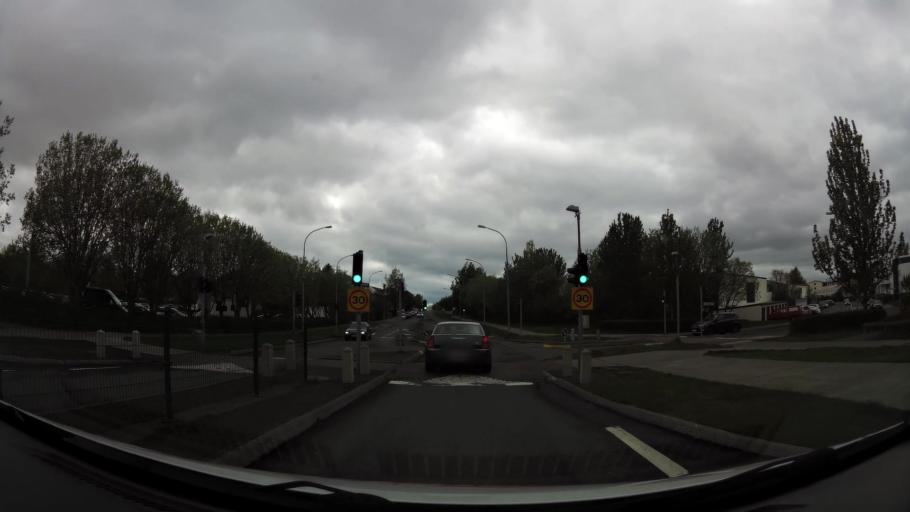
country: IS
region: Capital Region
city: Reykjavik
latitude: 64.1468
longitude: -21.8801
